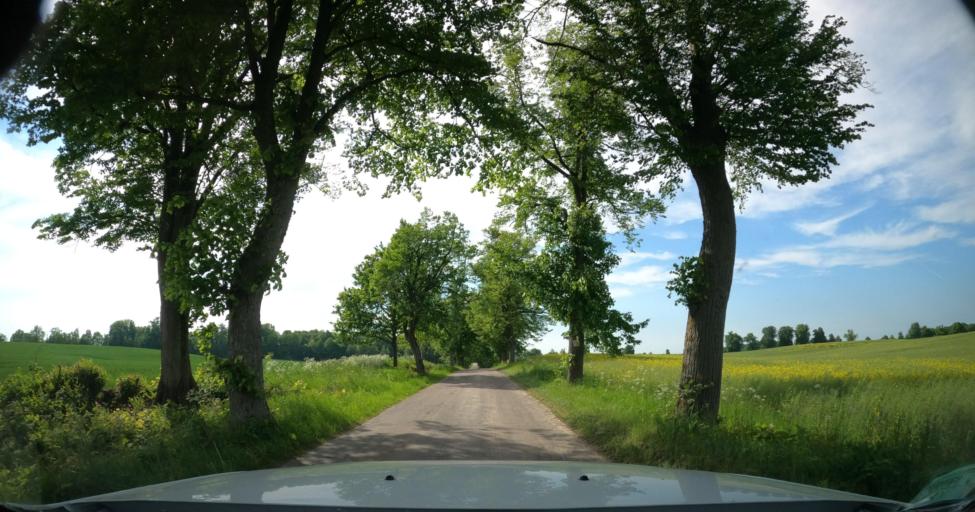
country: PL
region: Warmian-Masurian Voivodeship
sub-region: Powiat ostrodzki
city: Morag
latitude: 54.0178
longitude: 19.9203
